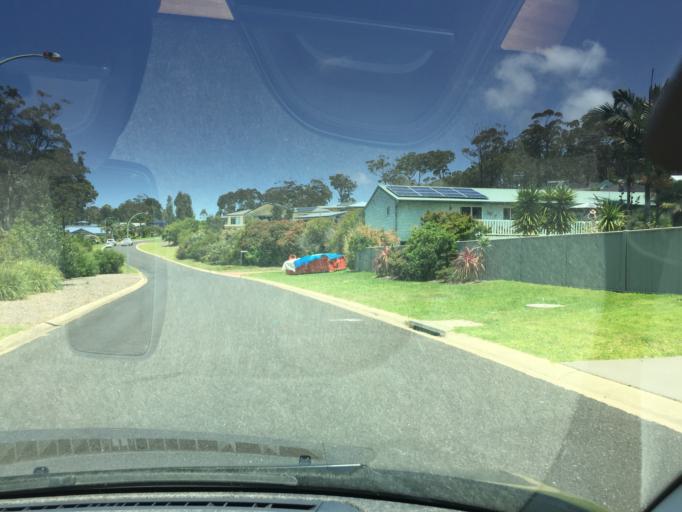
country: AU
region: New South Wales
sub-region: Bega Valley
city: Merimbula
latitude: -36.8493
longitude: 149.9270
